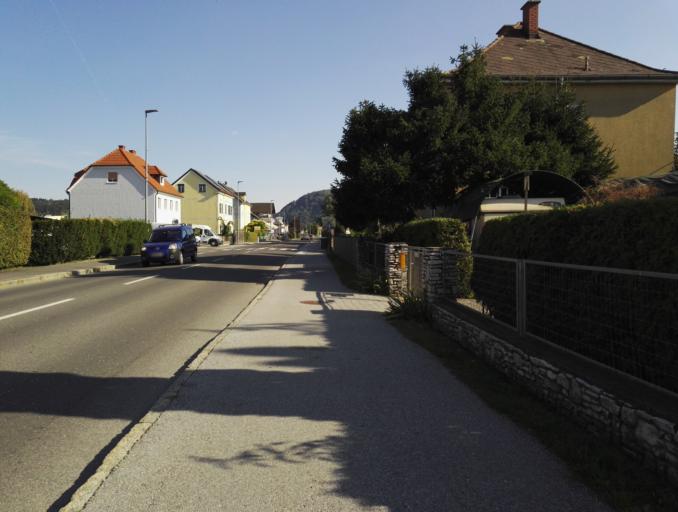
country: AT
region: Styria
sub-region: Politischer Bezirk Graz-Umgebung
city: Gratkorn
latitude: 47.1311
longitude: 15.3410
